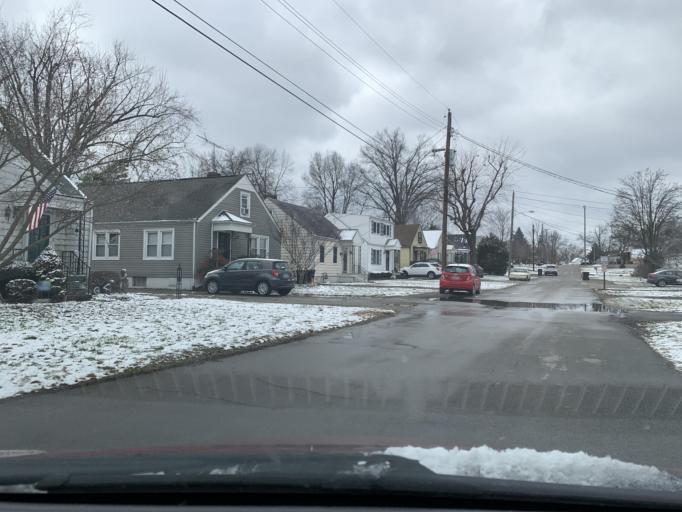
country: US
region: Kentucky
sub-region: Jefferson County
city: Audubon Park
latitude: 38.2211
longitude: -85.7348
